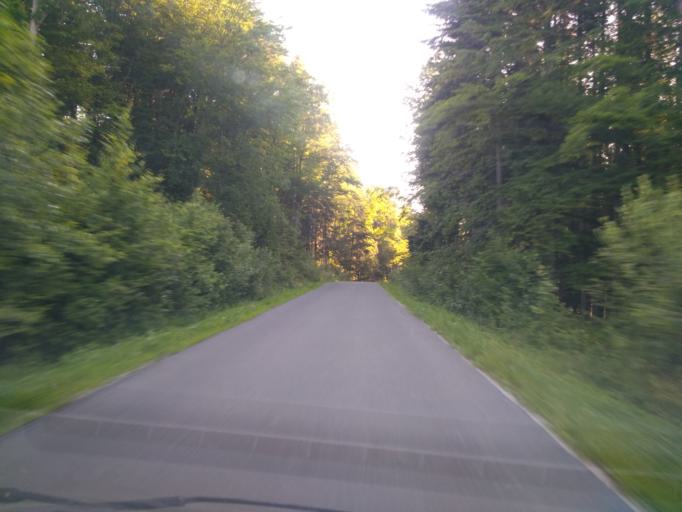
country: PL
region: Subcarpathian Voivodeship
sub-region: Powiat strzyzowski
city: Polomia
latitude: 49.9107
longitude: 21.9037
